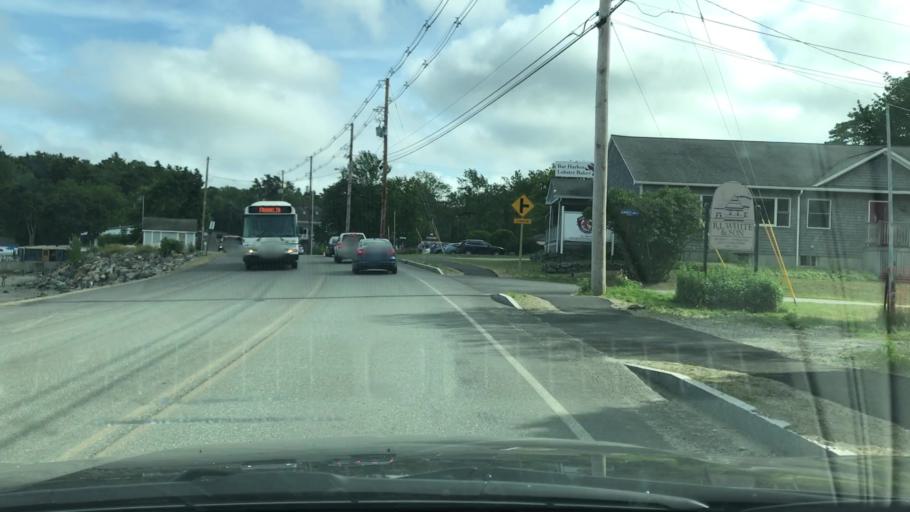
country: US
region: Maine
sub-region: Hancock County
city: Bar Harbor
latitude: 44.4152
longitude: -68.2512
